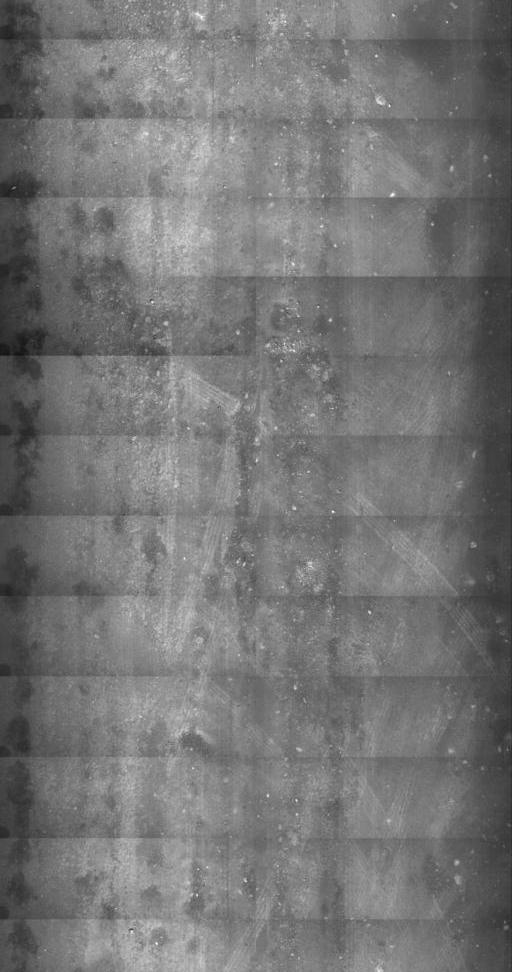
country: US
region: New Hampshire
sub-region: Grafton County
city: Lyme
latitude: 43.8319
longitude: -72.2474
